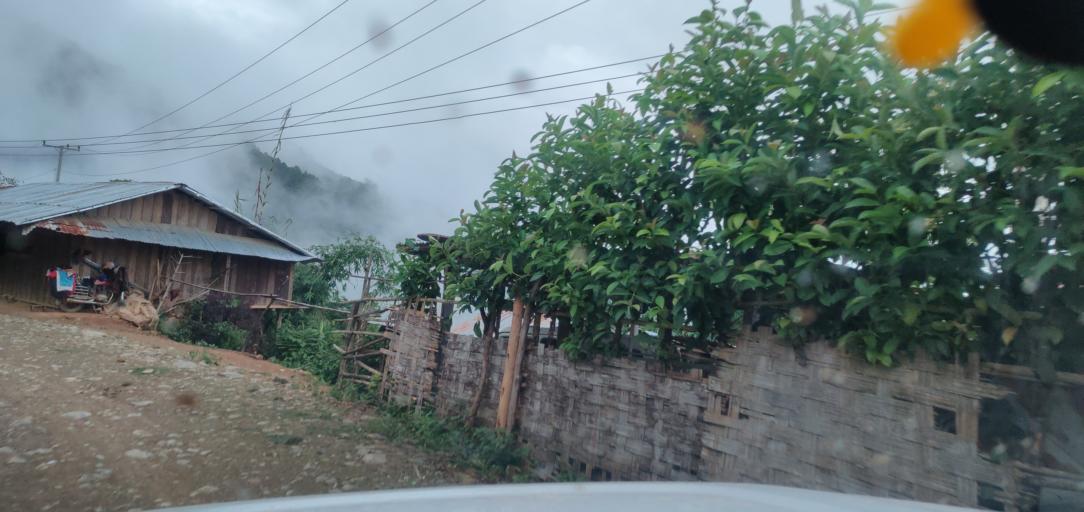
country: LA
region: Phongsali
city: Phongsali
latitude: 21.4408
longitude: 102.2952
